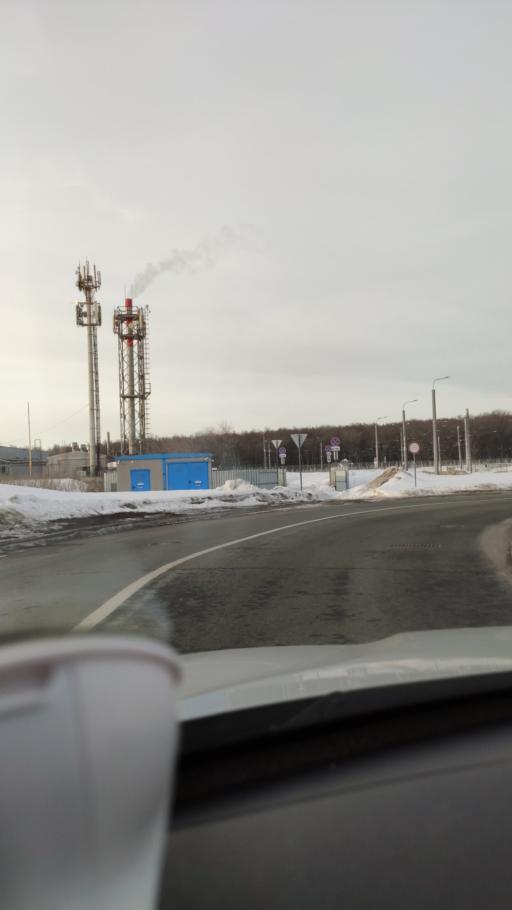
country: RU
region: Samara
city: Petra-Dubrava
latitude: 53.2724
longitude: 50.2563
